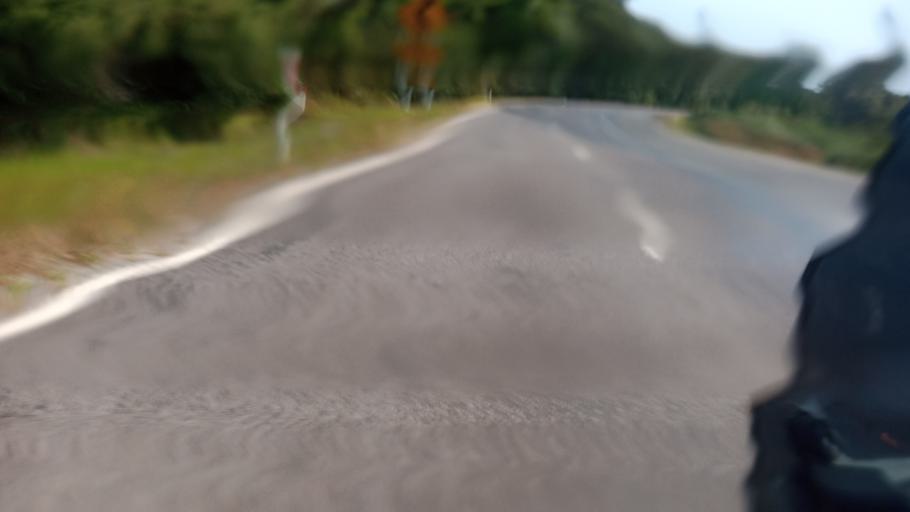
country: NZ
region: Bay of Plenty
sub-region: Opotiki District
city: Opotiki
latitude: -37.5743
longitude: 178.0847
